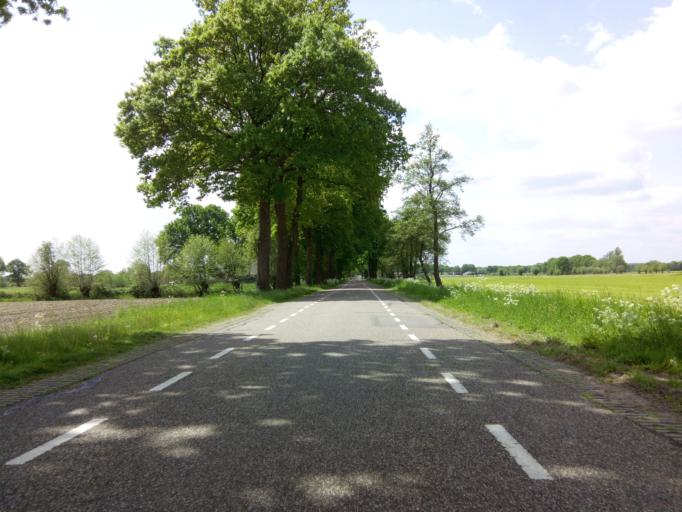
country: NL
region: Utrecht
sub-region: Gemeente Veenendaal
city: Veenendaal
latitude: 52.0594
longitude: 5.5383
